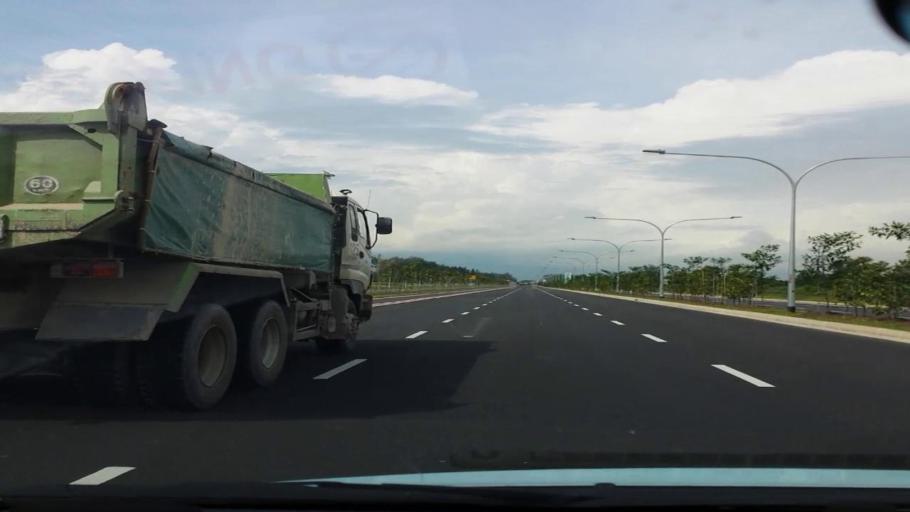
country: SG
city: Singapore
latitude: 1.3451
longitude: 104.0270
